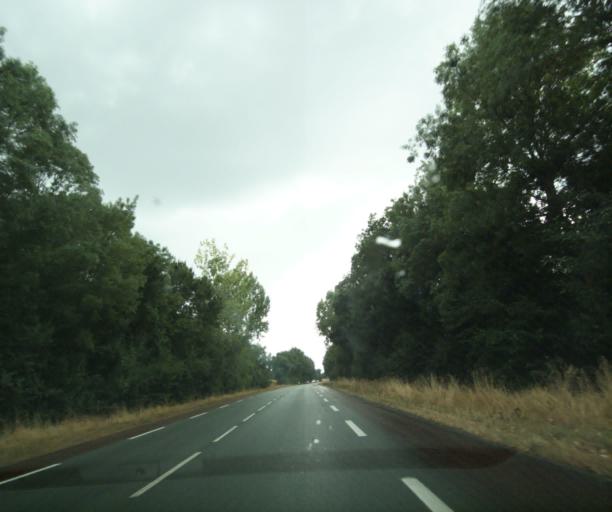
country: FR
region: Poitou-Charentes
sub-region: Departement de la Charente-Maritime
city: Cabariot
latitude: 45.9406
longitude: -0.8642
